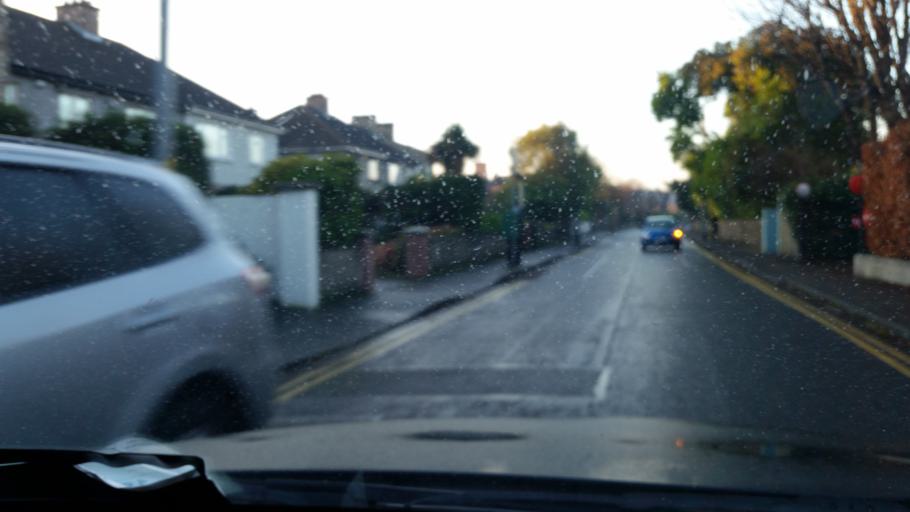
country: IE
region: Leinster
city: Sandymount
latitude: 53.3295
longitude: -6.2183
